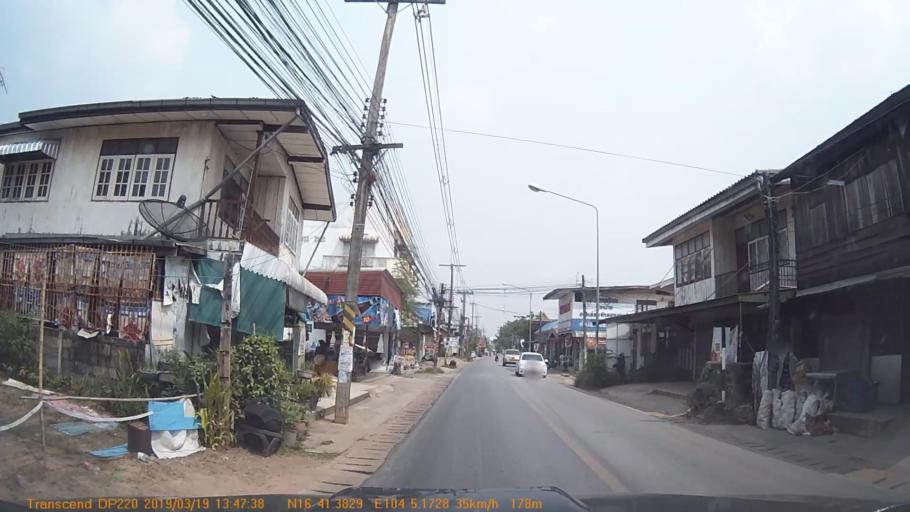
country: TH
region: Kalasin
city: Khao Wong
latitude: 16.6896
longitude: 104.0865
